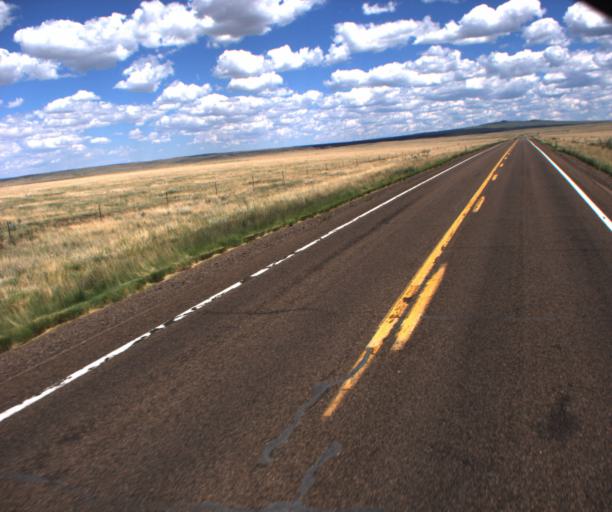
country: US
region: Arizona
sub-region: Apache County
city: Springerville
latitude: 34.1933
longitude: -109.3656
